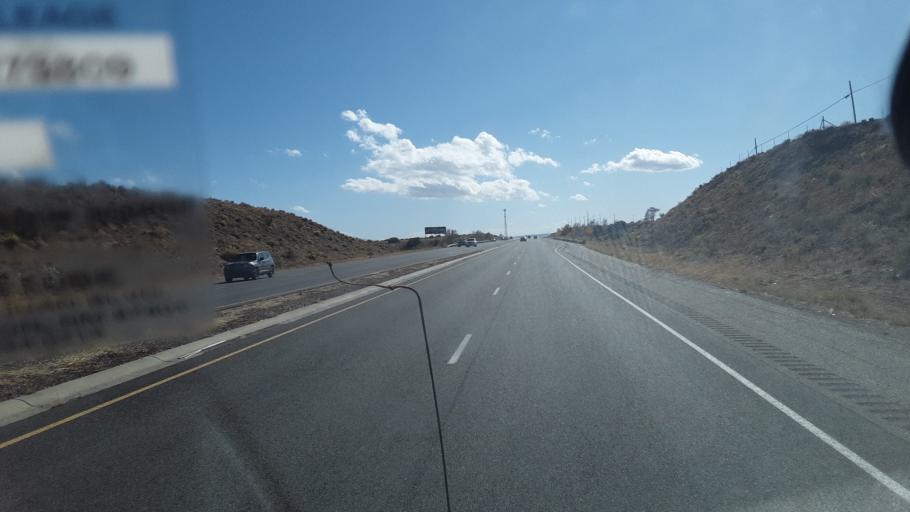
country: US
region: New Mexico
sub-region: Rio Arriba County
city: Ohkay Owingeh
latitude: 36.0255
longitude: -106.0924
